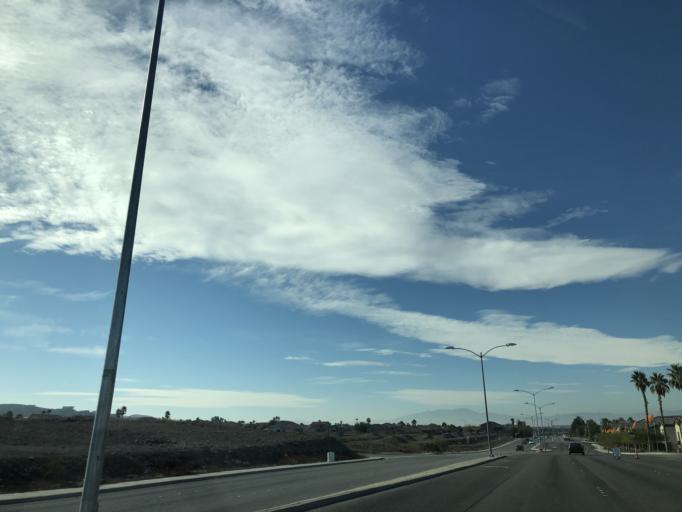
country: US
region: Nevada
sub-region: Clark County
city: Henderson
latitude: 36.0220
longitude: -115.0374
